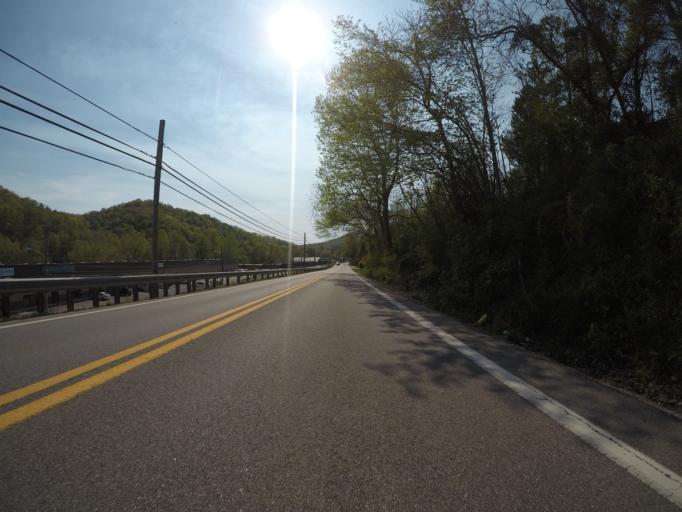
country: US
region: West Virginia
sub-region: Kanawha County
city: Pinch
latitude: 38.4055
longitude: -81.5305
